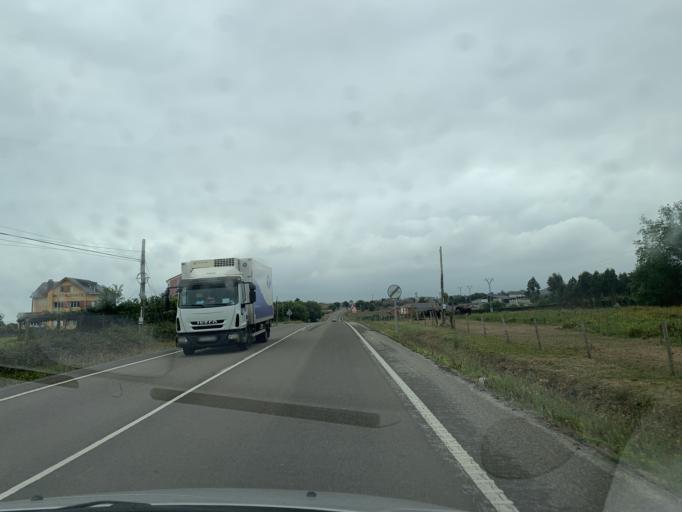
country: ES
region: Galicia
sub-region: Provincia de Lugo
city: Ribadeo
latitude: 43.5465
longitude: -7.1003
